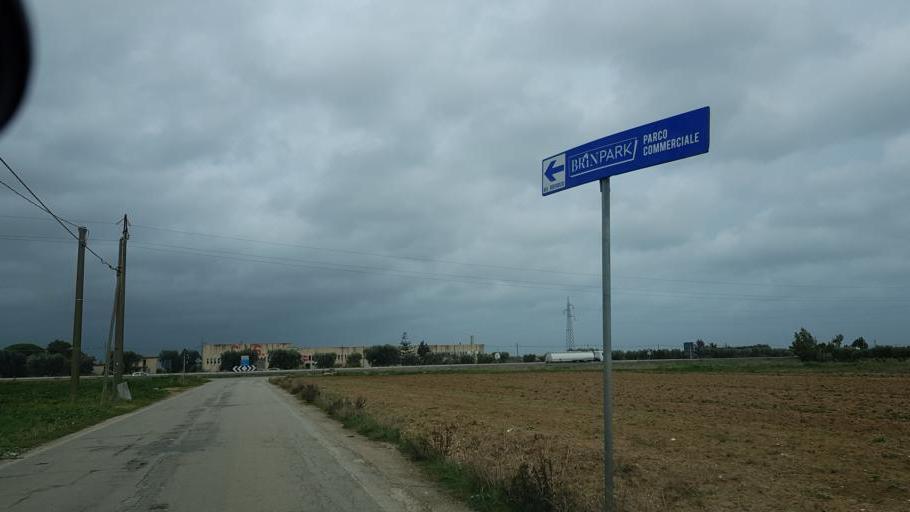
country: IT
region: Apulia
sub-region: Provincia di Brindisi
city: Brindisi
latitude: 40.6069
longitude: 17.8898
